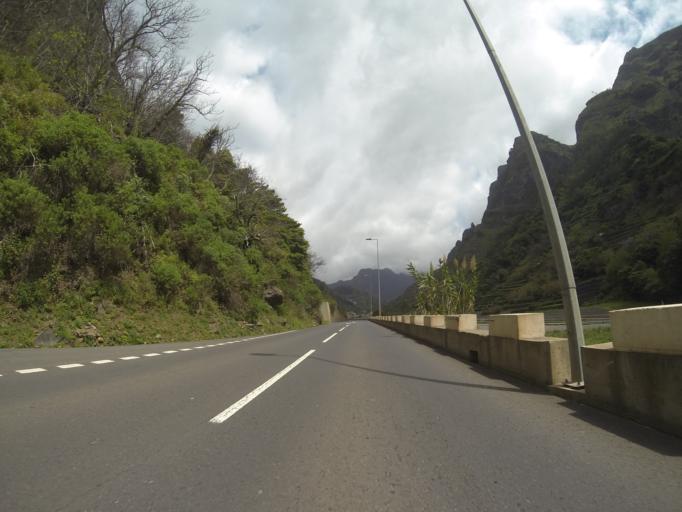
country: PT
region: Madeira
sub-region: Ribeira Brava
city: Campanario
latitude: 32.7147
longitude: -17.0337
